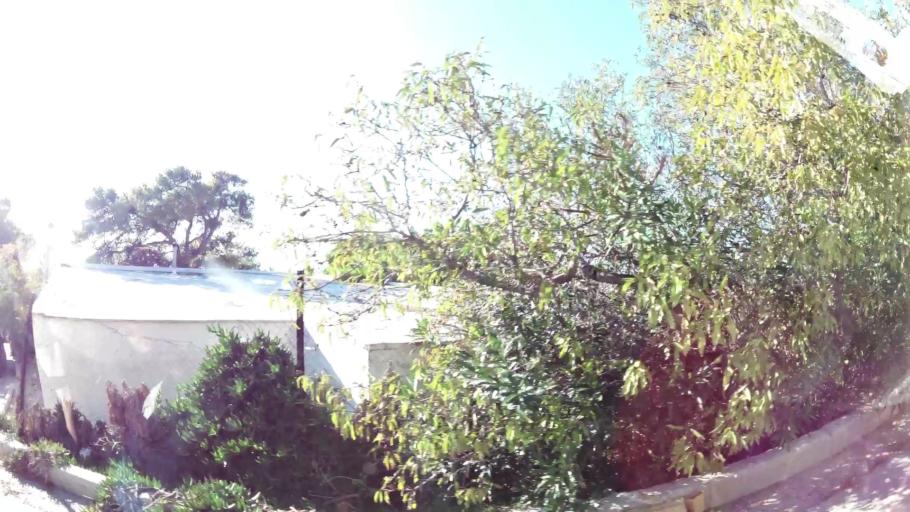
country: GR
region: Attica
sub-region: Nomarchia Athinas
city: Melissia
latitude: 38.0494
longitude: 23.8469
